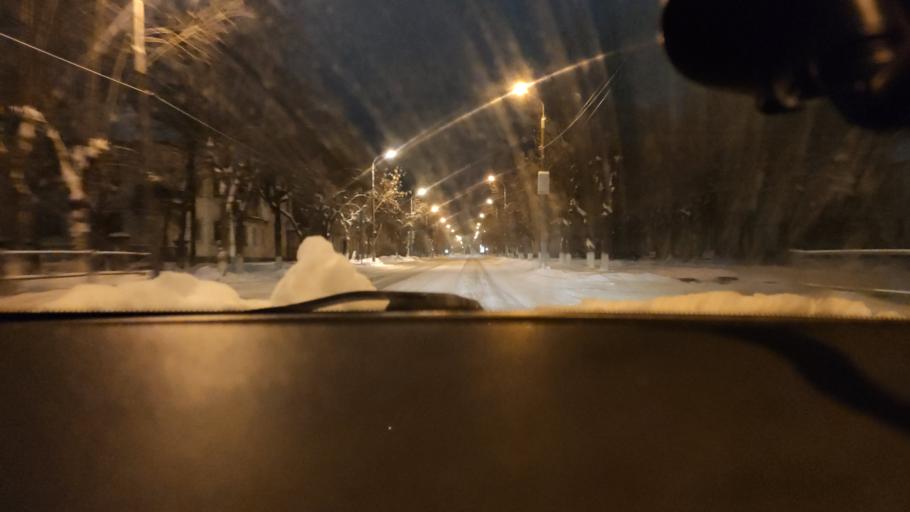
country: RU
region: Perm
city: Krasnokamsk
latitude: 58.0809
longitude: 55.7442
